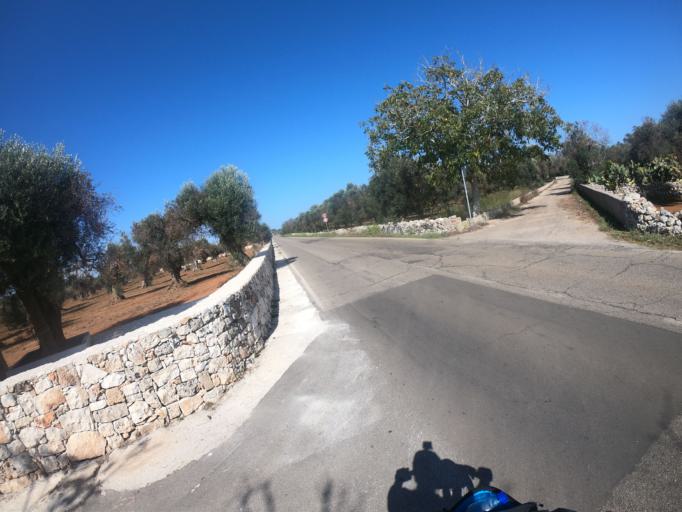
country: IT
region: Apulia
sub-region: Provincia di Lecce
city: Presicce
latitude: 39.9197
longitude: 18.2793
